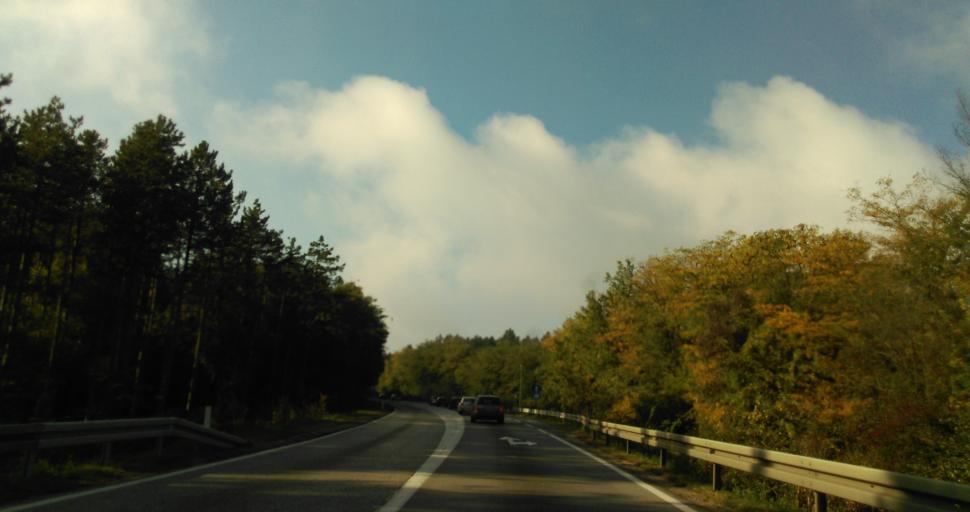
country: RS
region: Central Serbia
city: Sremcica
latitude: 44.6448
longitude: 20.4142
